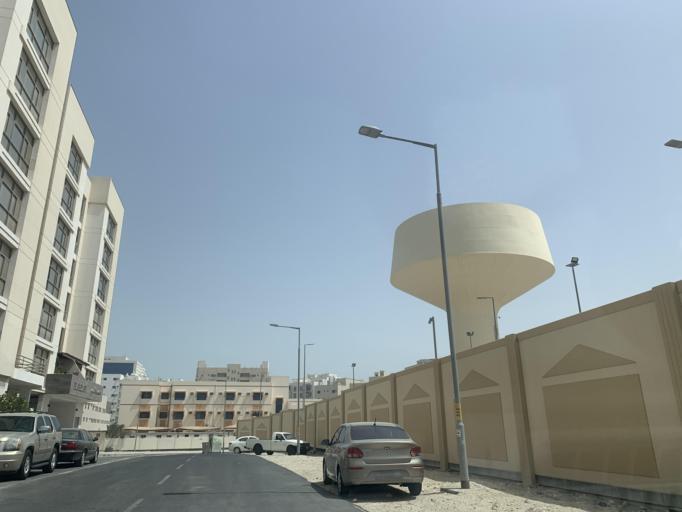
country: BH
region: Northern
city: Madinat `Isa
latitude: 26.1564
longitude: 50.5650
